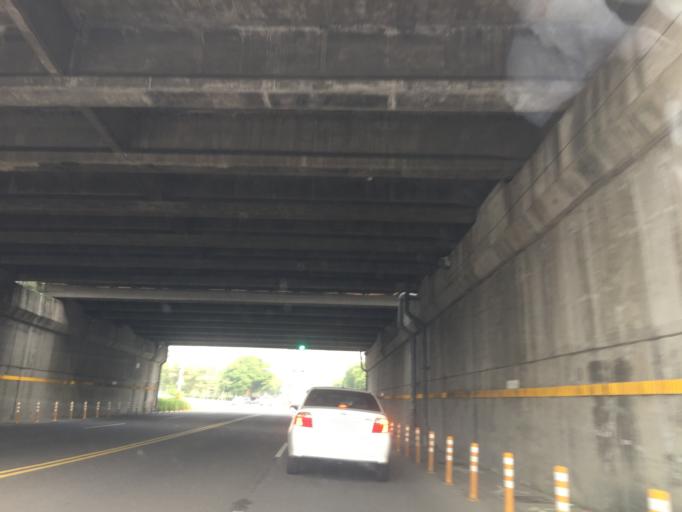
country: TW
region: Taiwan
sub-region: Hsinchu
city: Zhubei
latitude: 24.8208
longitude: 121.0149
